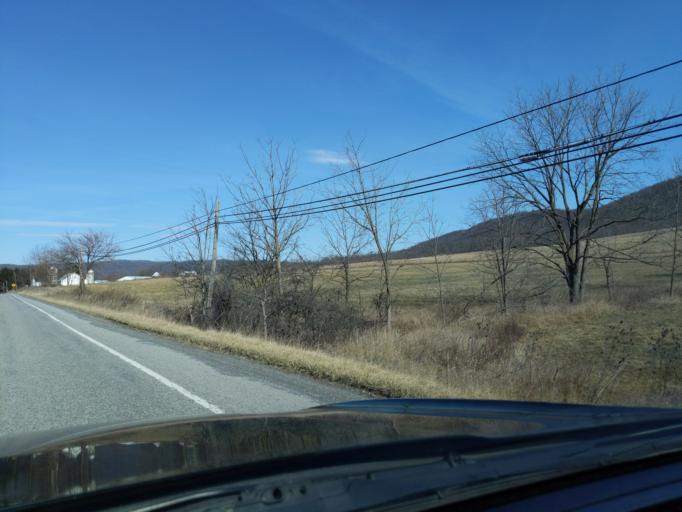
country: US
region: Pennsylvania
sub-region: Blair County
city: Roaring Spring
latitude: 40.3307
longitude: -78.3665
